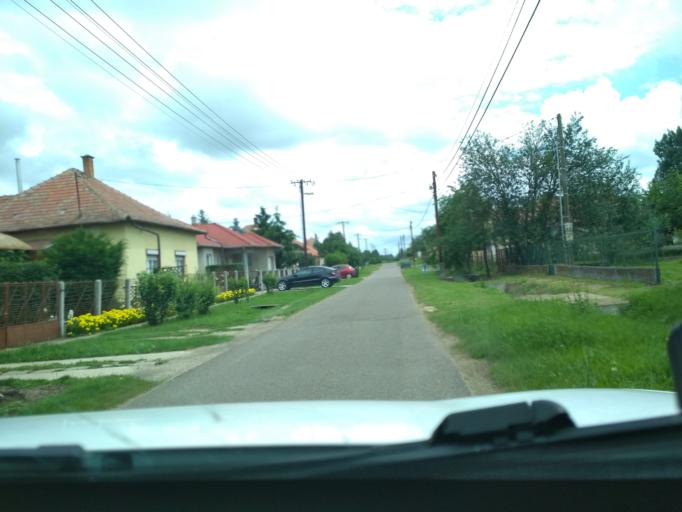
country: HU
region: Jasz-Nagykun-Szolnok
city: Tiszafured
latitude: 47.6040
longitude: 20.7229
